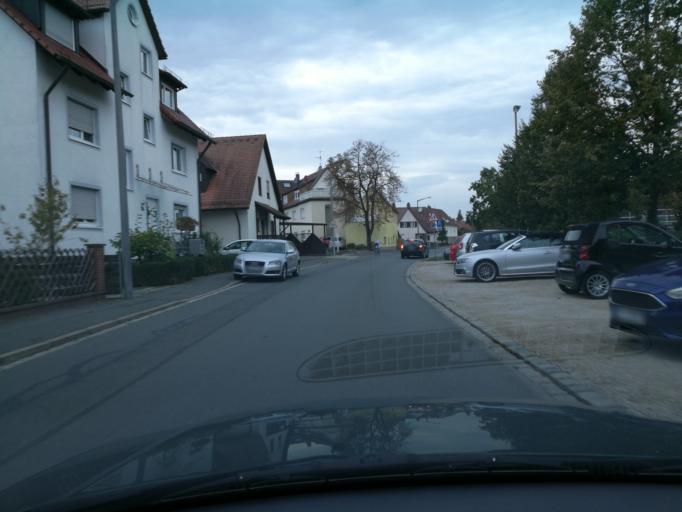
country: DE
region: Bavaria
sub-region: Regierungsbezirk Mittelfranken
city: Furth
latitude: 49.5245
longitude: 11.0122
